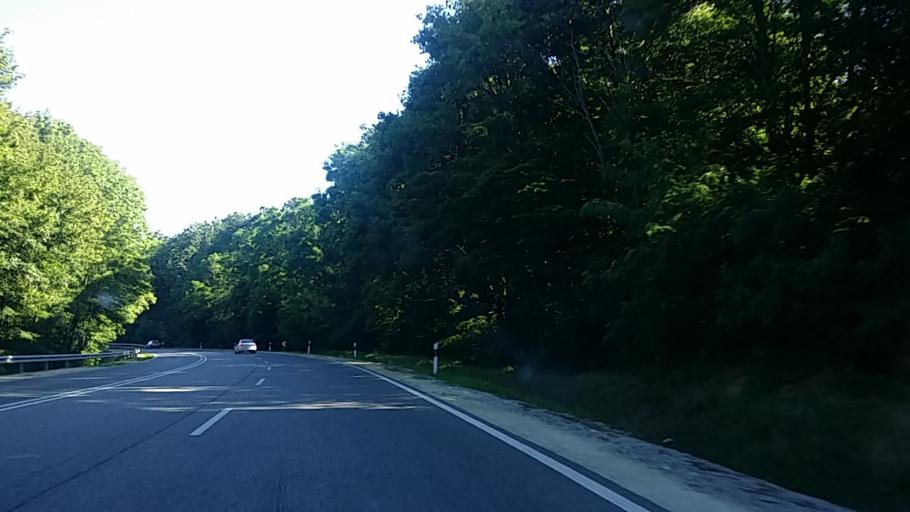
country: HU
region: Zala
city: Pacsa
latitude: 46.8260
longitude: 17.0535
